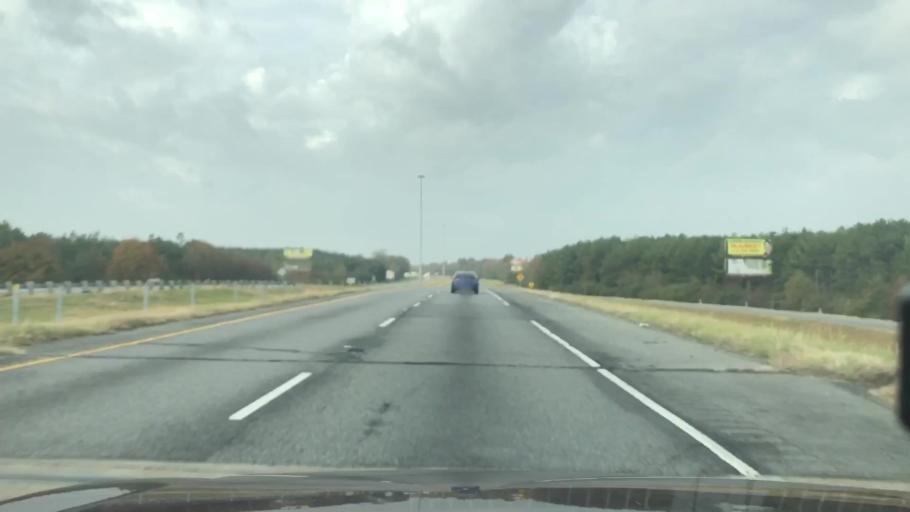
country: US
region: Louisiana
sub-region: Richland Parish
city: Delhi
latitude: 32.4432
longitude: -91.4943
